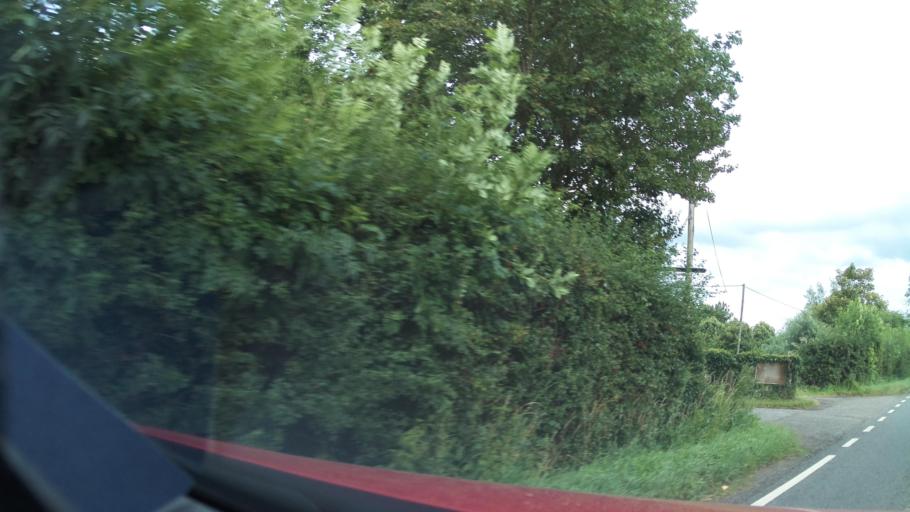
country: GB
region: England
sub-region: Warwickshire
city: Dunchurch
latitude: 52.3098
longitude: -1.3125
